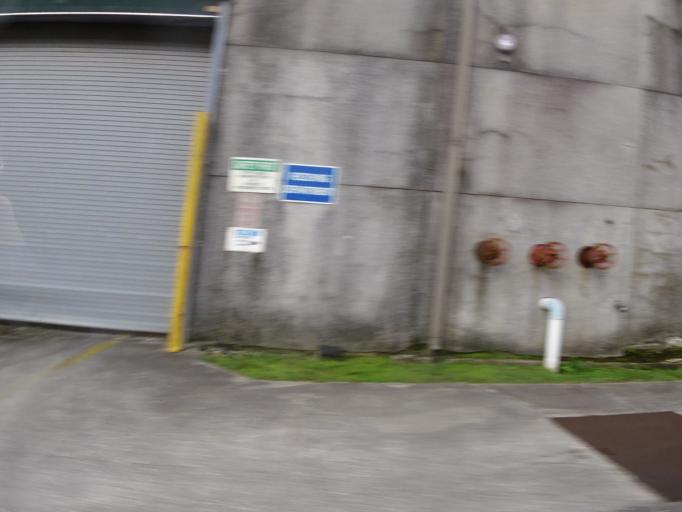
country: US
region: Florida
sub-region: Duval County
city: Jacksonville
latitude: 30.3554
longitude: -81.6267
